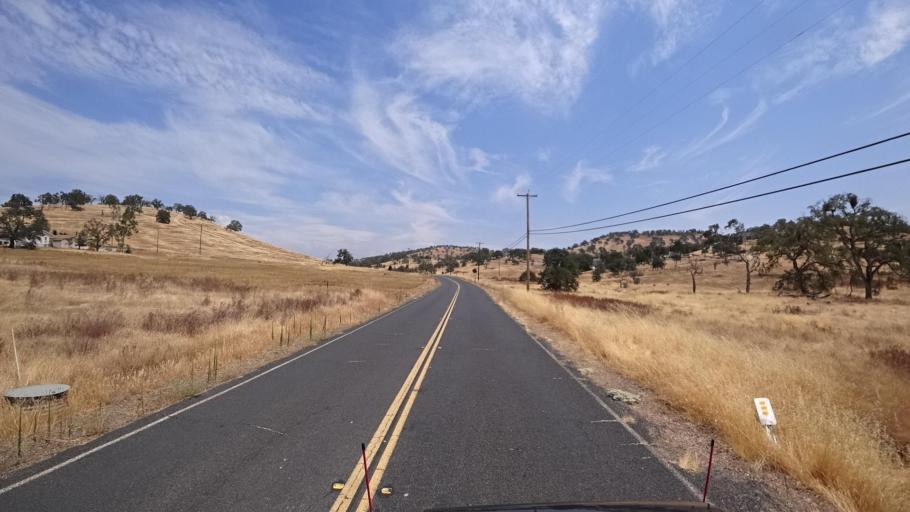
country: US
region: California
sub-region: Tuolumne County
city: Jamestown
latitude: 37.6709
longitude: -120.3658
